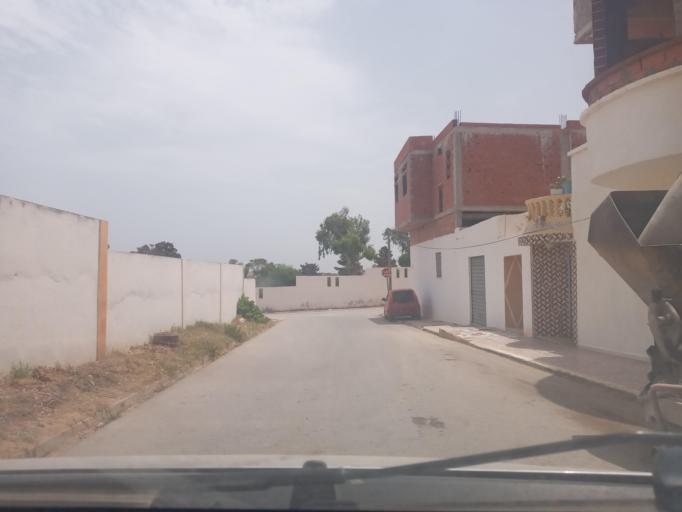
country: TN
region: Nabul
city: El Haouaria
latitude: 37.0534
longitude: 11.0087
